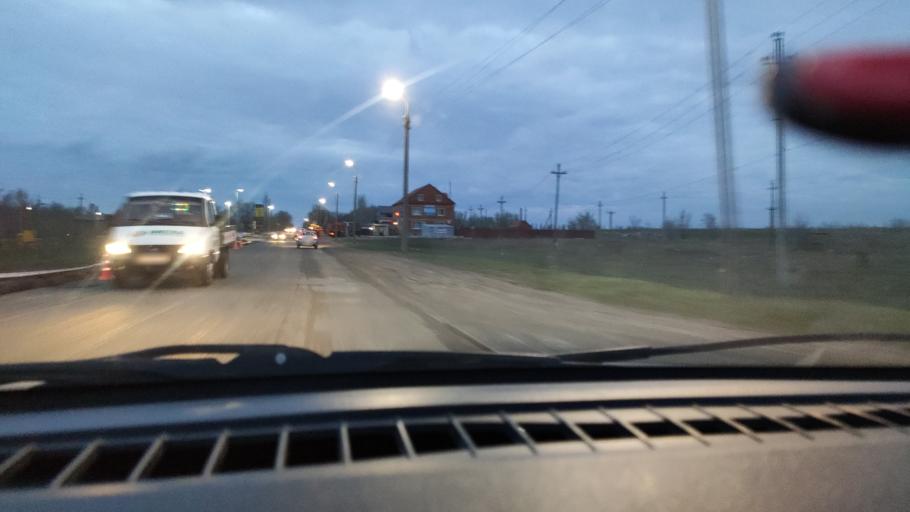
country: RU
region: Orenburg
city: Tatarskaya Kargala
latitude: 51.8692
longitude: 55.1432
